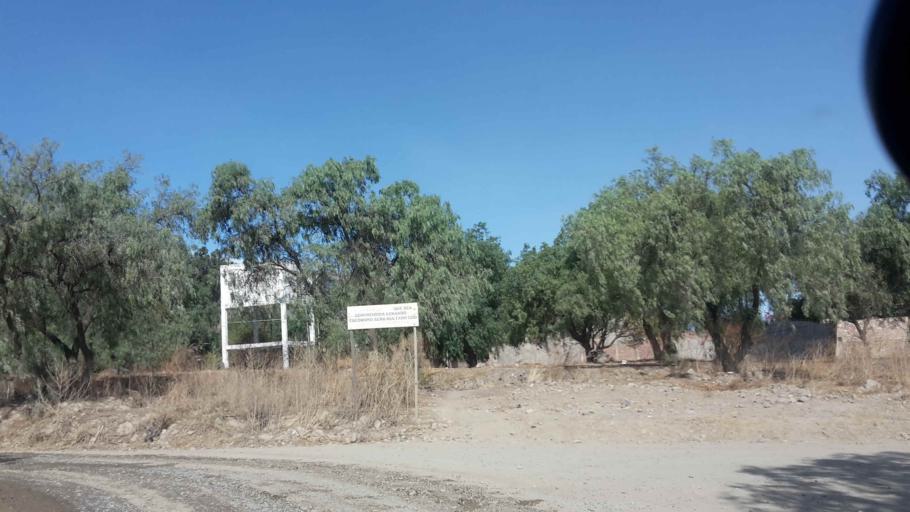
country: BO
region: Cochabamba
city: Cochabamba
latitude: -17.3387
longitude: -66.2120
